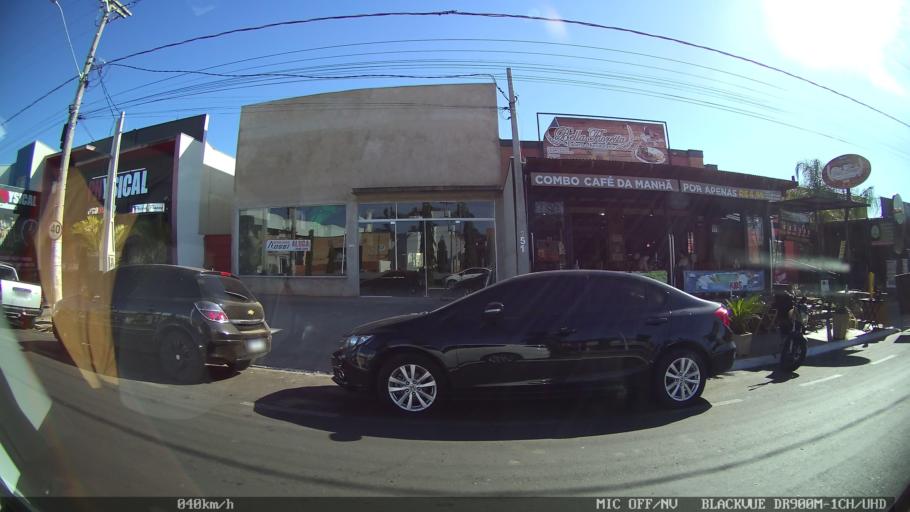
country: BR
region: Sao Paulo
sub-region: Olimpia
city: Olimpia
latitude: -20.7320
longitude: -48.9130
